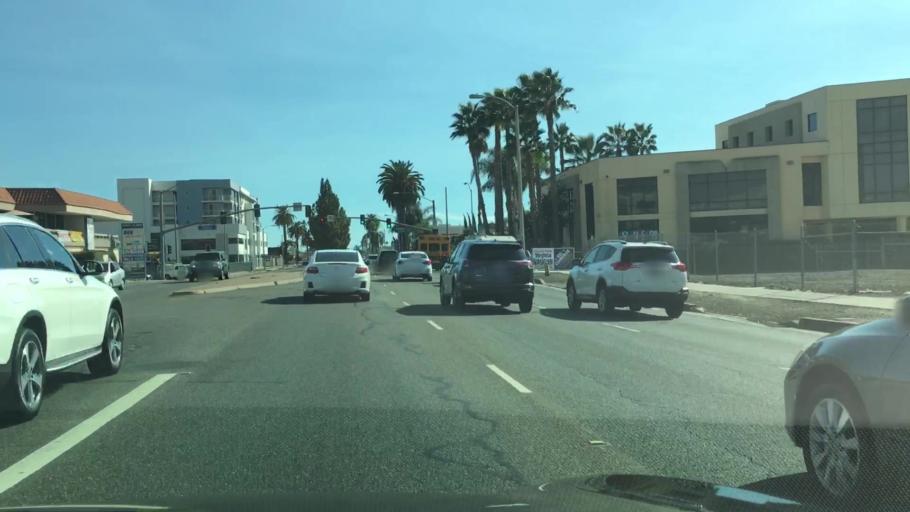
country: US
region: California
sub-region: Orange County
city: Buena Park
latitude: 33.8778
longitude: -117.9984
